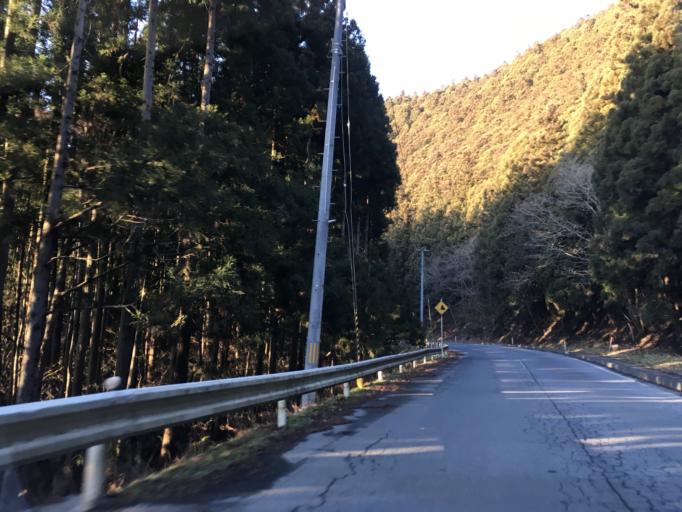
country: JP
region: Iwate
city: Ichinoseki
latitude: 38.8038
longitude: 141.2310
